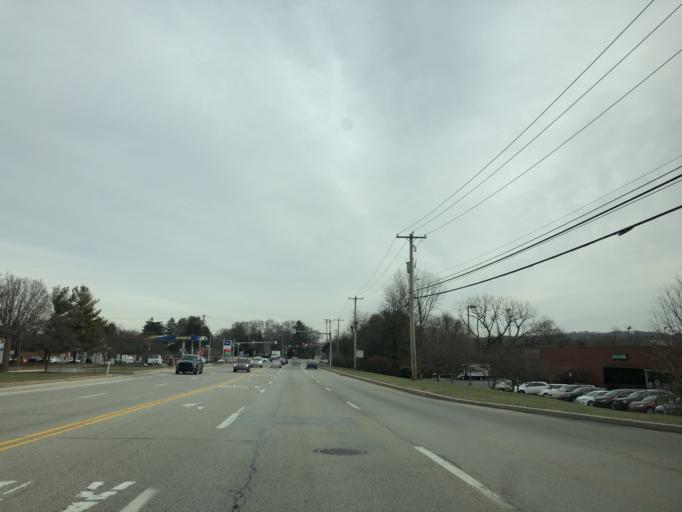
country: US
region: Pennsylvania
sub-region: Chester County
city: Exton
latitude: 40.0246
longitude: -75.6474
